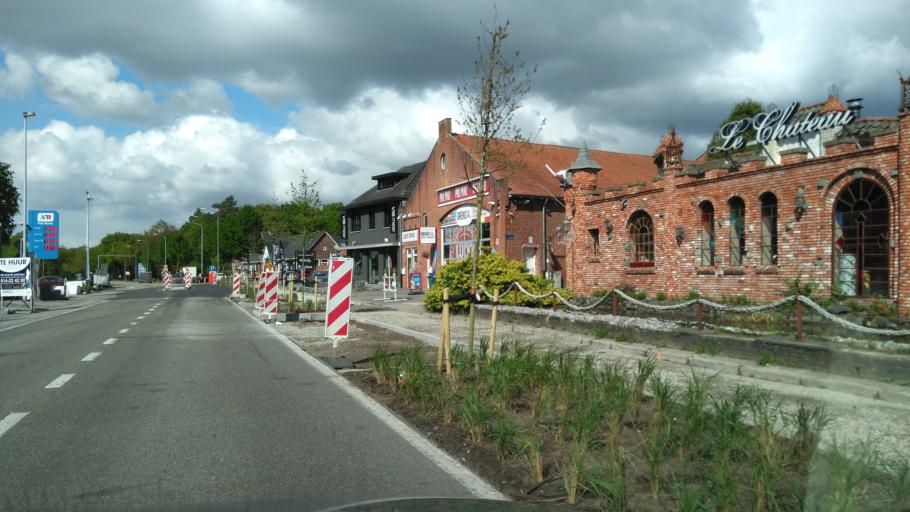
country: NL
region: North Brabant
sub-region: Gemeente Goirle
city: Goirle
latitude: 51.4703
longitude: 5.0481
